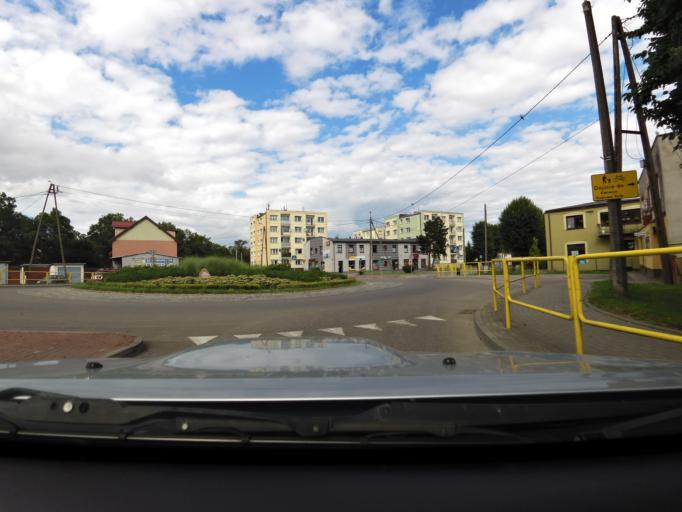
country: PL
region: Pomeranian Voivodeship
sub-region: Powiat nowodworski
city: Nowy Dwor Gdanski
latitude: 54.2078
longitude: 19.1174
